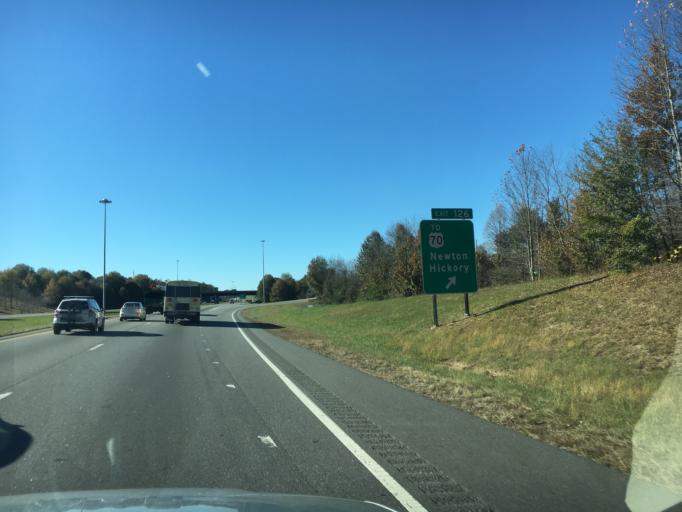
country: US
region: North Carolina
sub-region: Catawba County
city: Hickory
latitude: 35.7076
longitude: -81.2896
